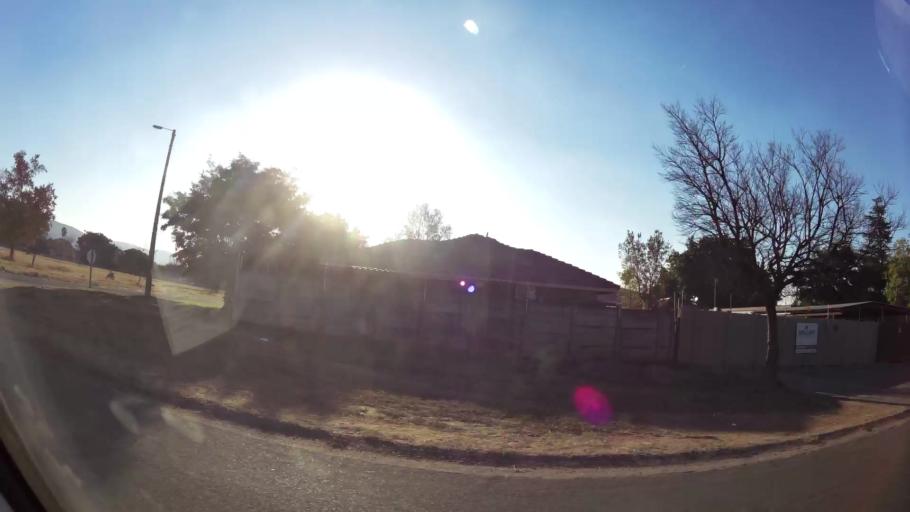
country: ZA
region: North-West
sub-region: Bojanala Platinum District Municipality
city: Rustenburg
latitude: -25.6791
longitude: 27.2291
